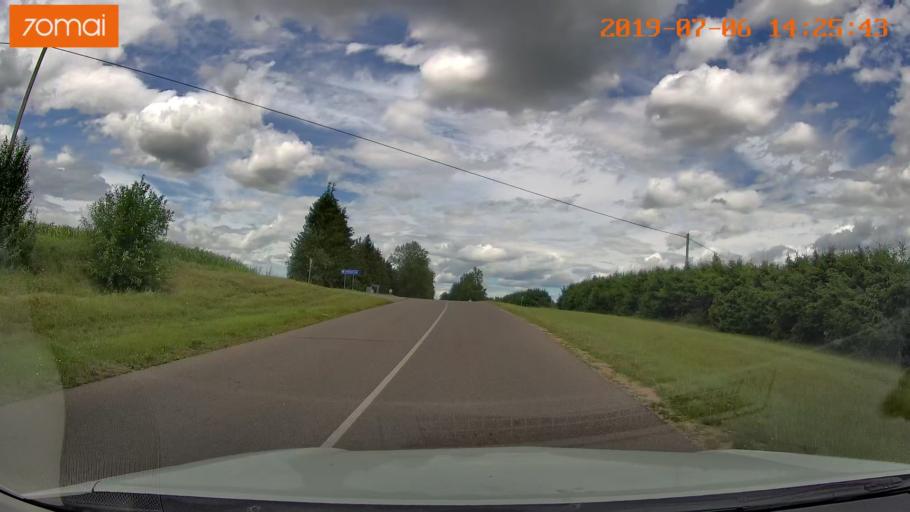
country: BY
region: Minsk
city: Ivyanyets
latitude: 53.9321
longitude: 26.7949
